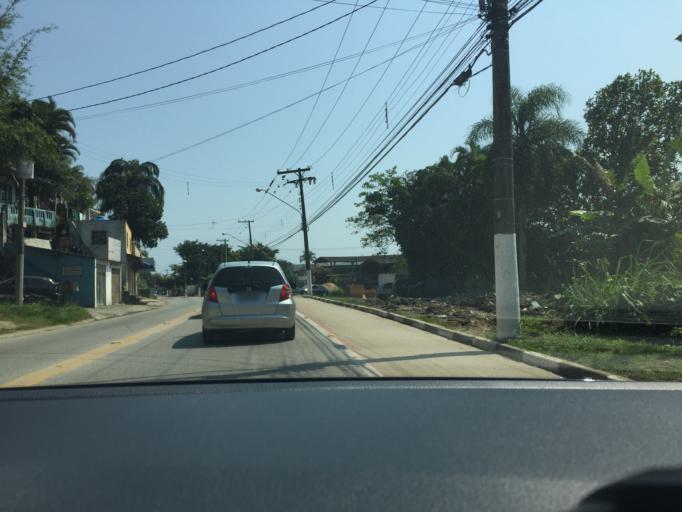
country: BR
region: Sao Paulo
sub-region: Guaruja
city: Guaruja
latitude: -23.9793
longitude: -46.1911
